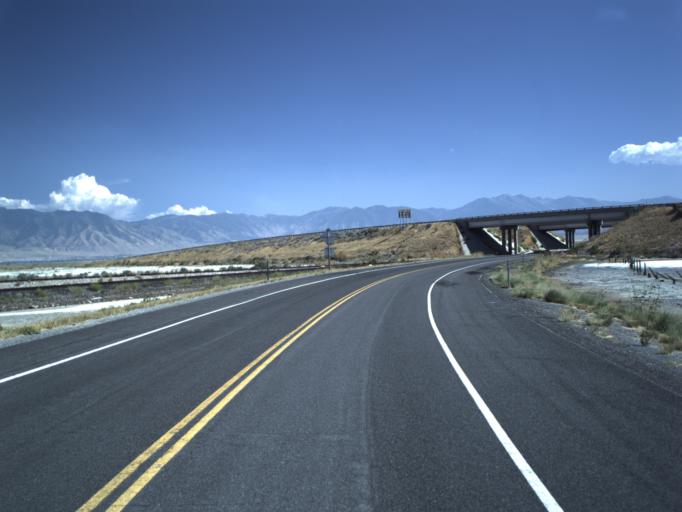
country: US
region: Utah
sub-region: Tooele County
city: Grantsville
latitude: 40.6862
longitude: -112.4423
